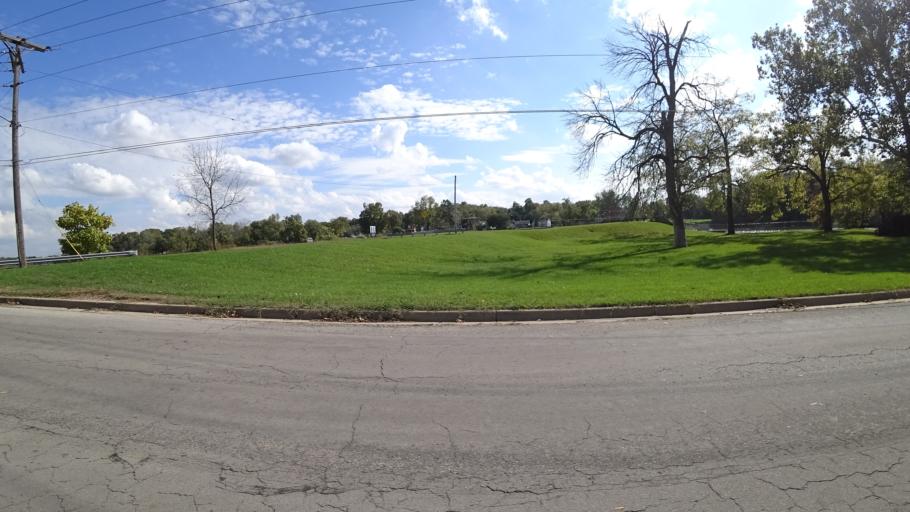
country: US
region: Michigan
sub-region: Saint Joseph County
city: Three Rivers
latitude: 41.9419
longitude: -85.6252
